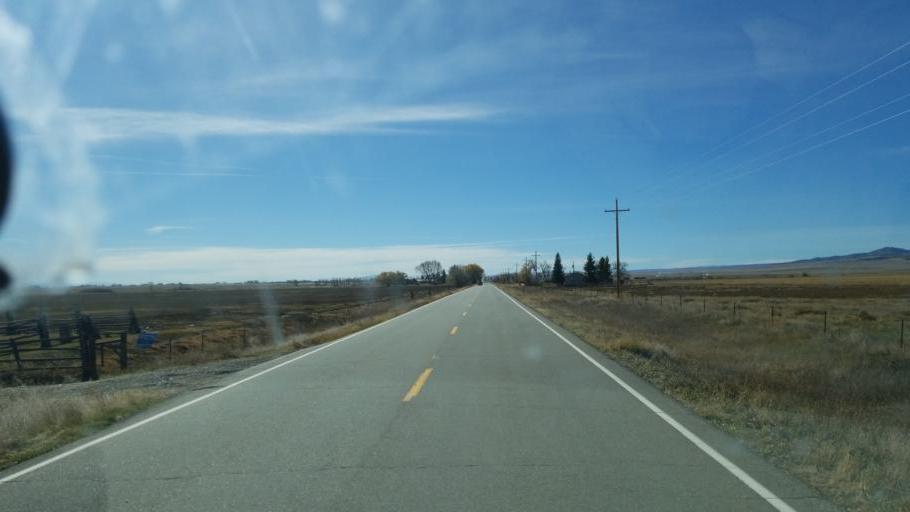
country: US
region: Colorado
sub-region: Rio Grande County
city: Monte Vista
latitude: 37.4936
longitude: -106.1490
